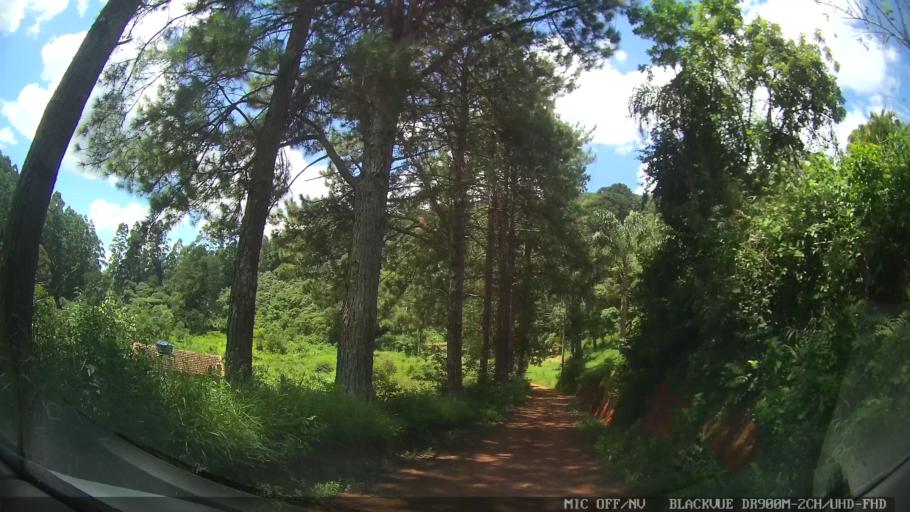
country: BR
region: Minas Gerais
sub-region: Extrema
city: Extrema
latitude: -22.8896
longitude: -46.2958
